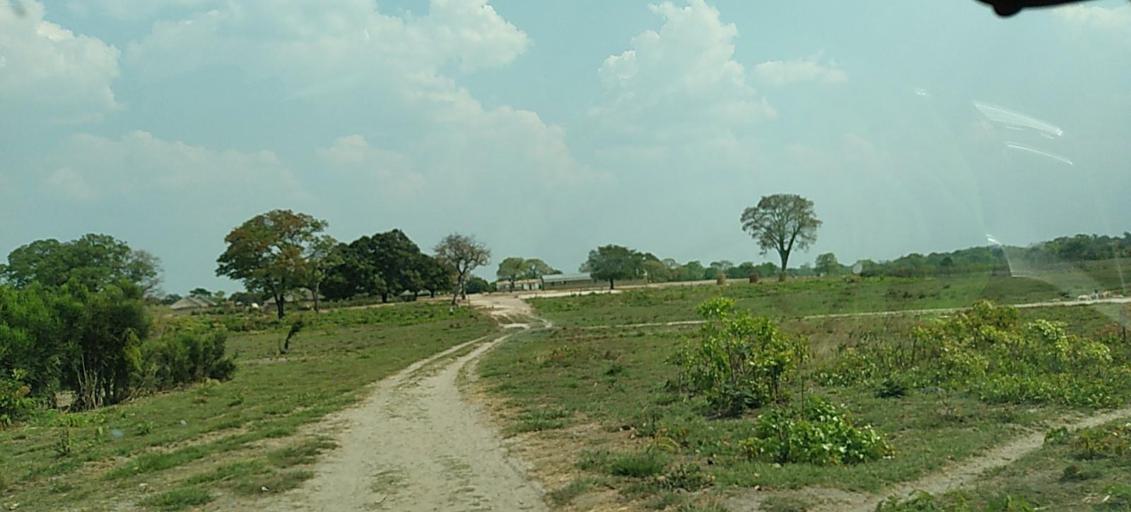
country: ZM
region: North-Western
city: Kabompo
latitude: -13.4477
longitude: 23.6674
